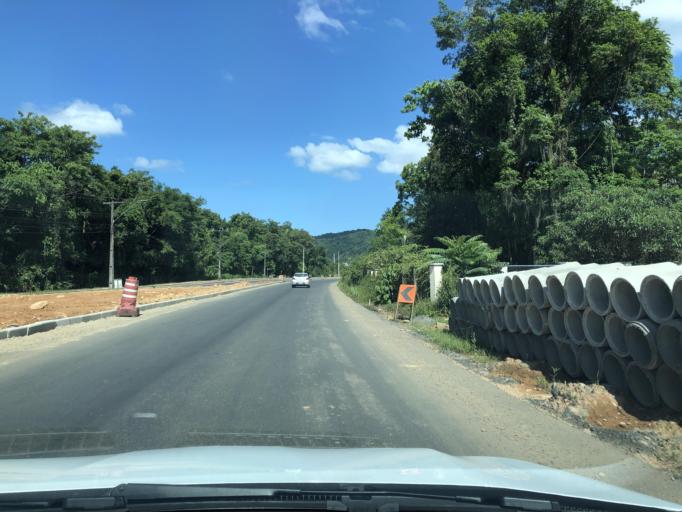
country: BR
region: Santa Catarina
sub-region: Joinville
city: Joinville
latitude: -26.2496
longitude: -48.8565
